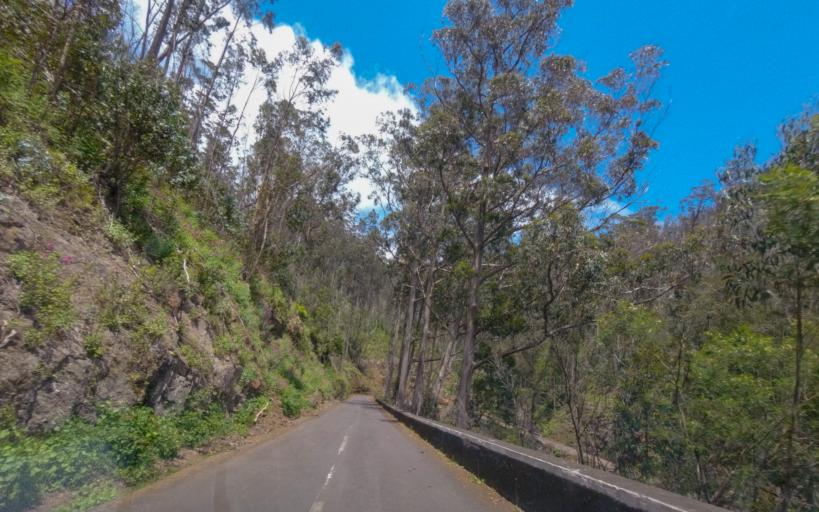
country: PT
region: Madeira
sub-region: Funchal
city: Nossa Senhora do Monte
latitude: 32.6796
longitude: -16.8811
